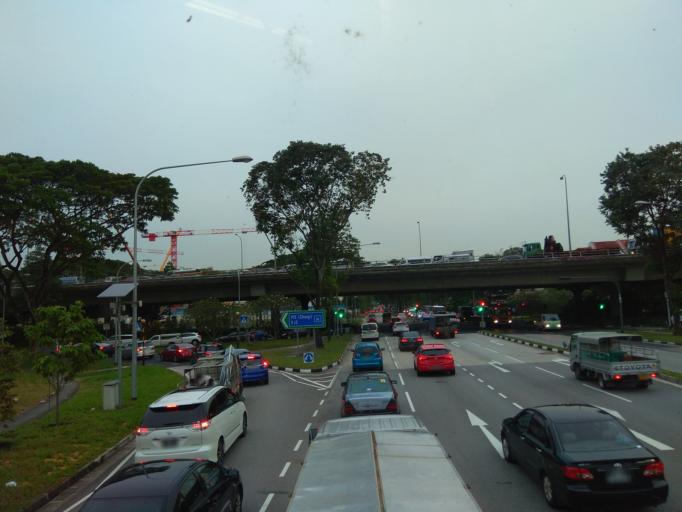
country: MY
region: Johor
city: Johor Bahru
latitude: 1.3555
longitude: 103.6973
